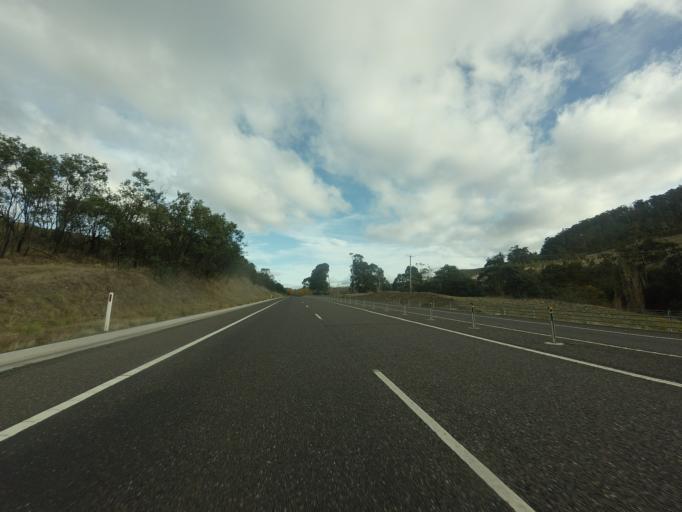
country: AU
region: Tasmania
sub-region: Brighton
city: Bridgewater
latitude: -42.5556
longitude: 147.2099
